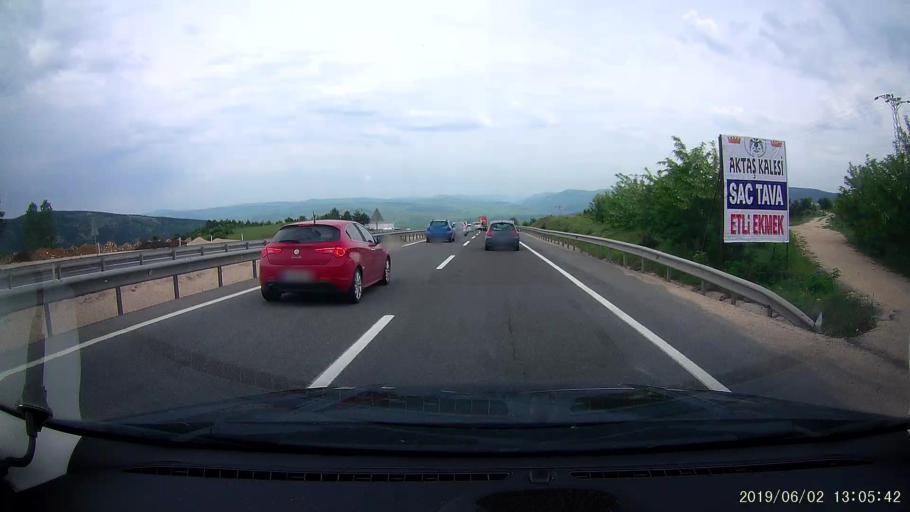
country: TR
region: Karabuk
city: Gozyeri
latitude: 40.8598
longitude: 32.5433
